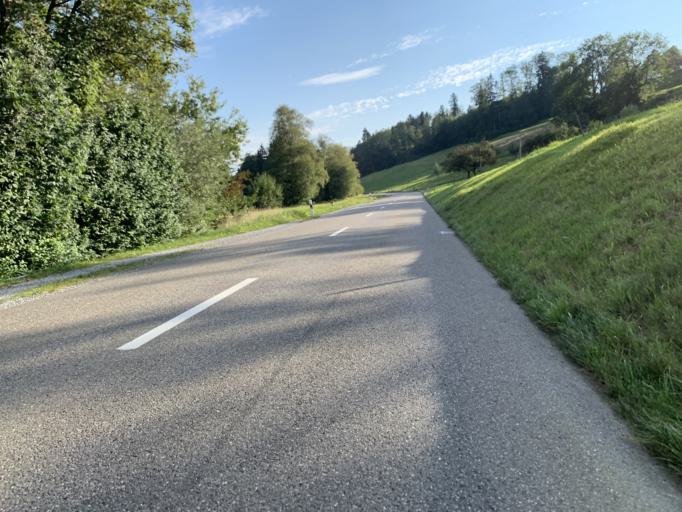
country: CH
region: Zurich
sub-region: Bezirk Hinwil
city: Hinwil
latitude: 47.3131
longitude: 8.8539
